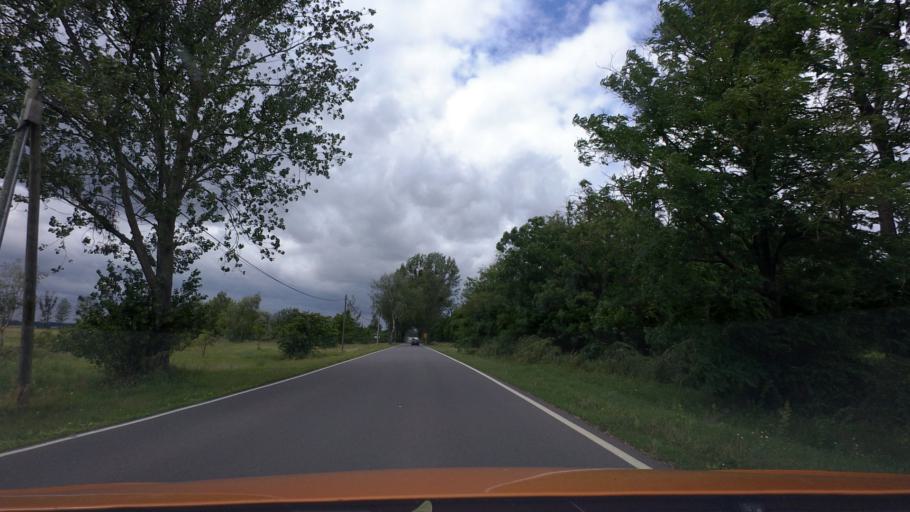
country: DE
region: Brandenburg
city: Neulewin
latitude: 52.7026
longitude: 14.2625
